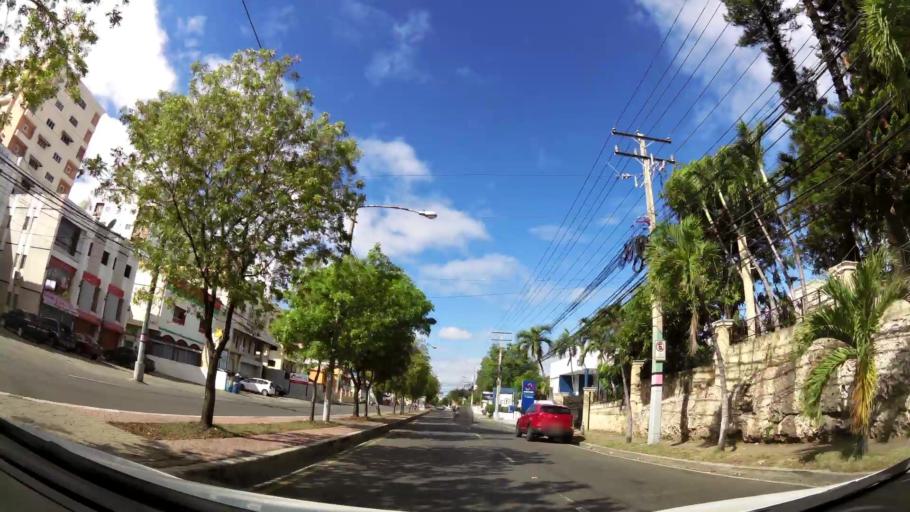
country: DO
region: Nacional
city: Bella Vista
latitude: 18.4561
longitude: -69.9422
